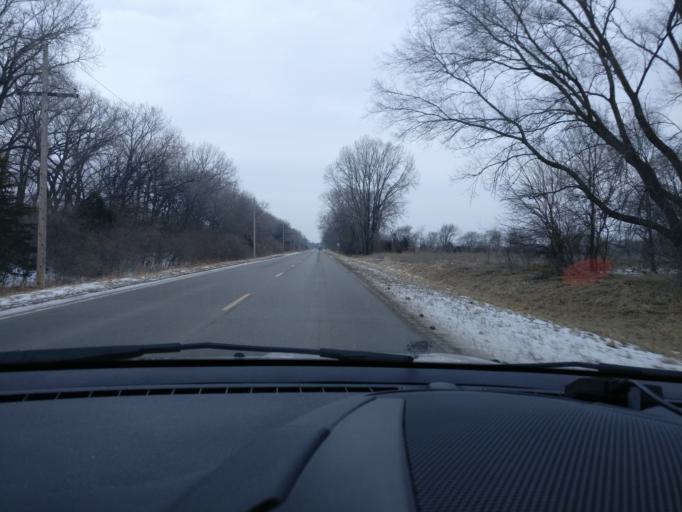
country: US
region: Nebraska
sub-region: Dodge County
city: Fremont
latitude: 41.4430
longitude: -96.5368
